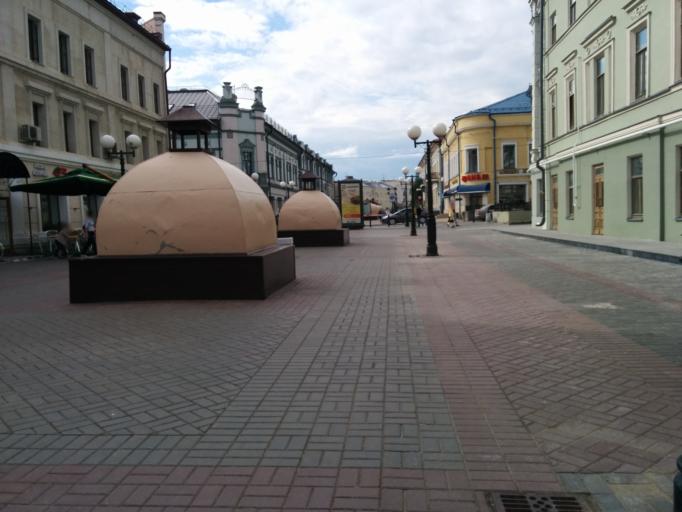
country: RU
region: Tatarstan
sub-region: Gorod Kazan'
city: Kazan
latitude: 55.7926
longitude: 49.1112
